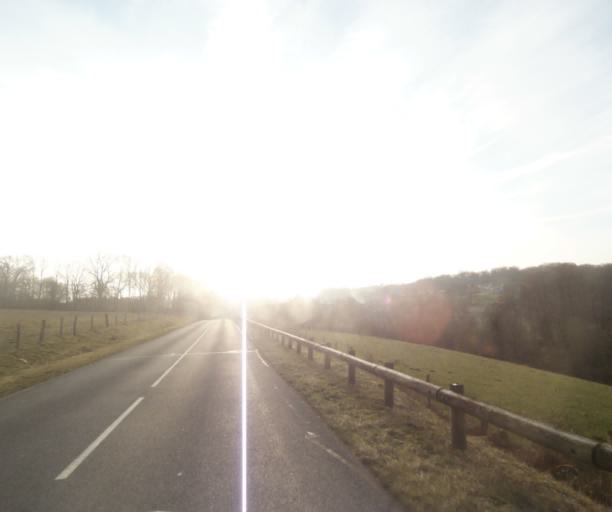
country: FR
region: Champagne-Ardenne
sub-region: Departement de la Marne
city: Sermaize-les-Bains
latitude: 48.7254
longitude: 4.9378
